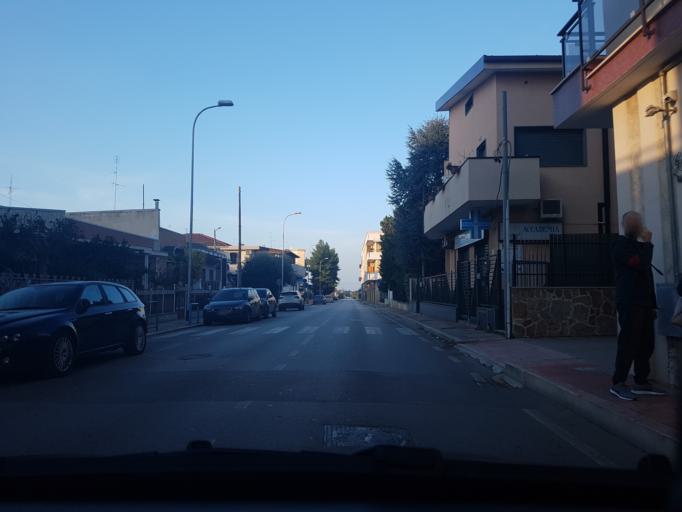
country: IT
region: Apulia
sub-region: Provincia di Bari
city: Bitritto
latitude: 41.0453
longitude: 16.8270
